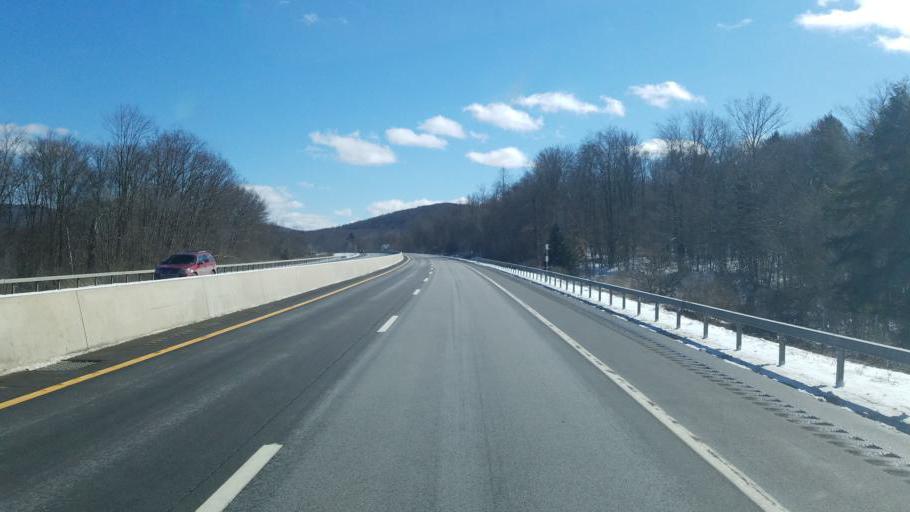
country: US
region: New York
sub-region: Cattaraugus County
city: Salamanca
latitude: 42.1050
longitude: -78.6626
